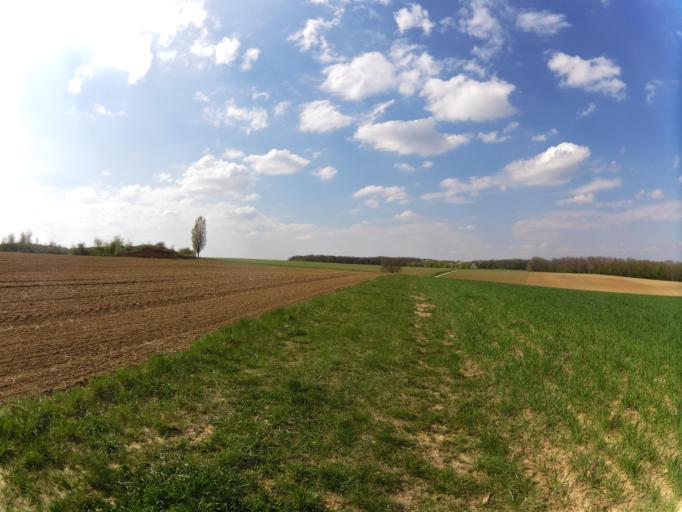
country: DE
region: Bavaria
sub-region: Regierungsbezirk Unterfranken
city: Winterhausen
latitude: 49.6902
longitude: 10.0143
